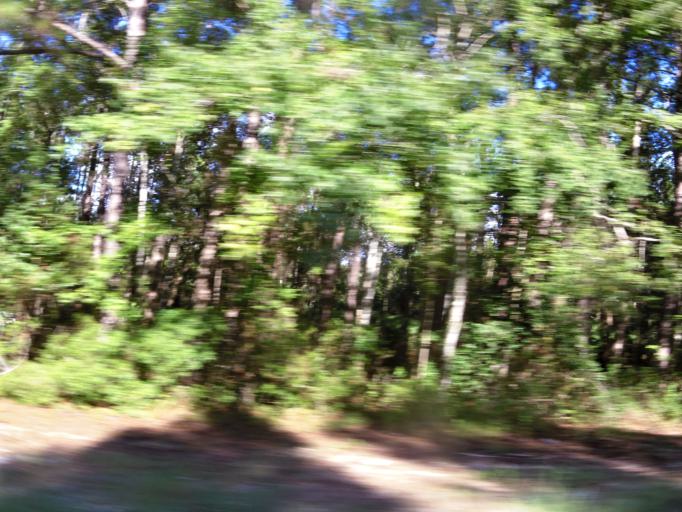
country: US
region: Georgia
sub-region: Camden County
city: Woodbine
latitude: 31.0614
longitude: -81.7287
